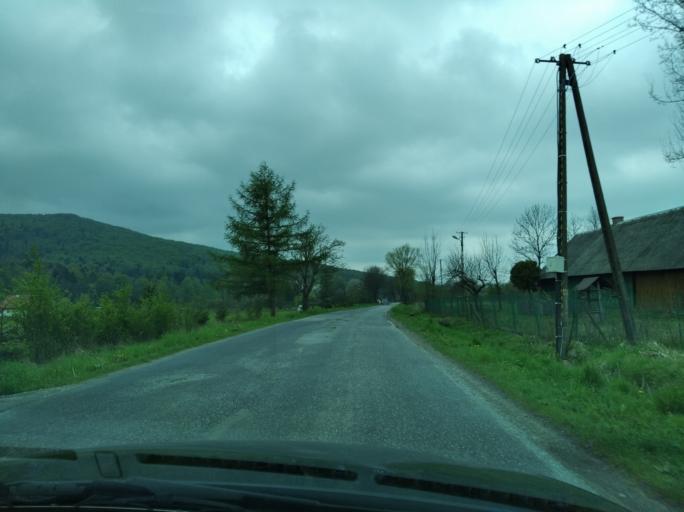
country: PL
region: Subcarpathian Voivodeship
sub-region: Powiat sanocki
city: Sanok
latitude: 49.6153
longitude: 22.2654
